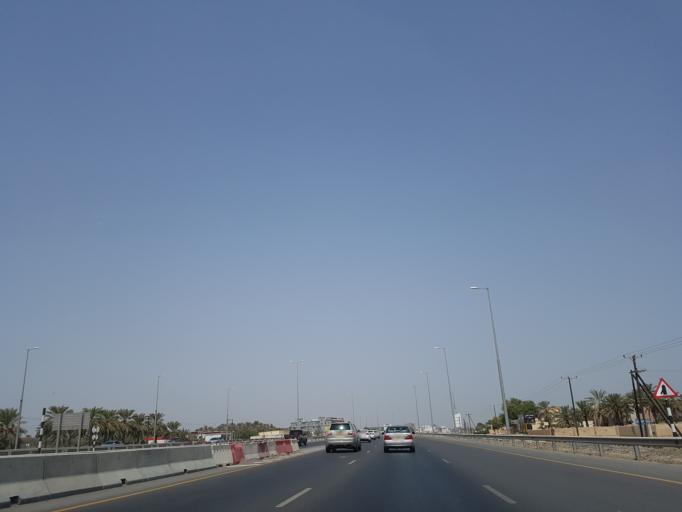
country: OM
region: Al Batinah
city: Saham
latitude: 24.1344
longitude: 56.8871
